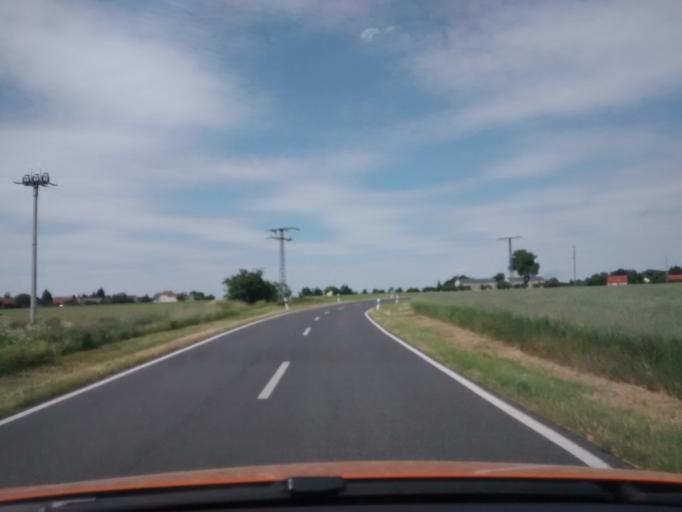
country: DE
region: Brandenburg
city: Ihlow
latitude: 51.9194
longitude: 13.3261
